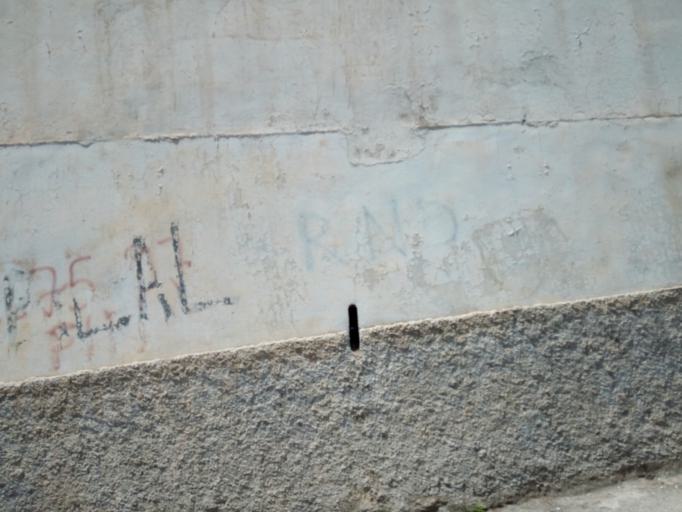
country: DZ
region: Constantine
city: Constantine
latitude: 36.3712
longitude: 6.6198
